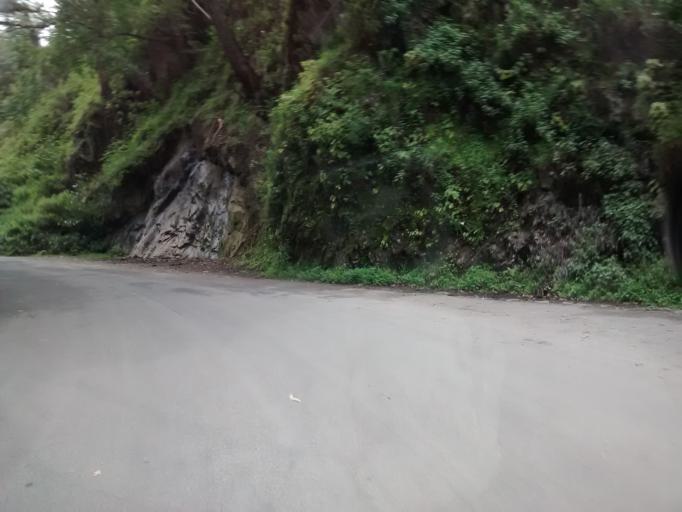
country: IN
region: Kerala
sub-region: Idukki
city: Munnar
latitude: 10.1165
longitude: 77.1504
